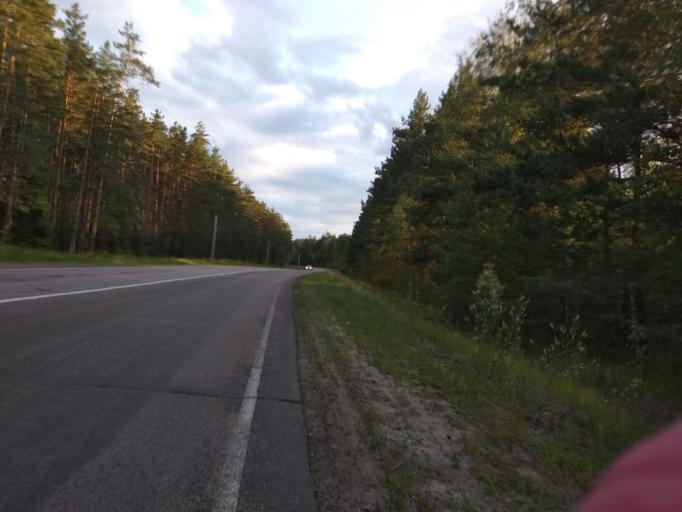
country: RU
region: Moskovskaya
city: Misheronskiy
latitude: 55.6267
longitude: 39.7383
